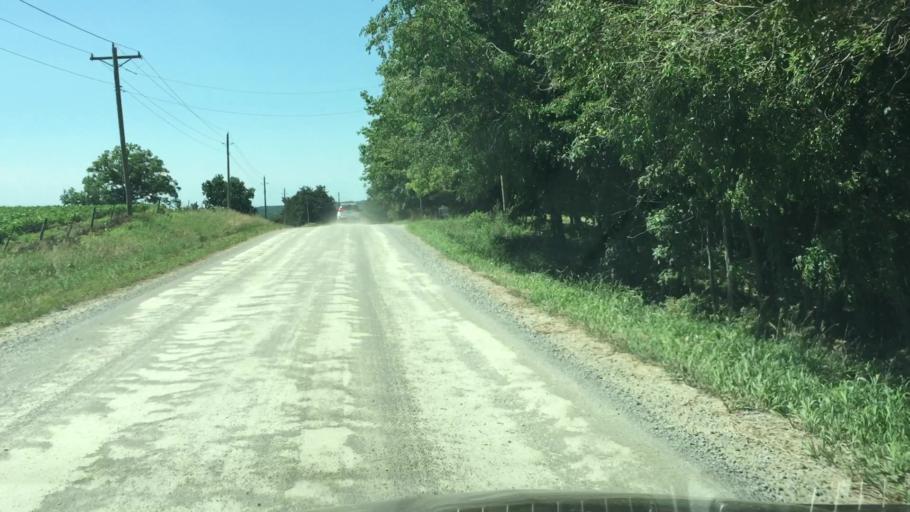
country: US
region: Iowa
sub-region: Linn County
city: Ely
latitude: 41.8314
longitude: -91.5897
